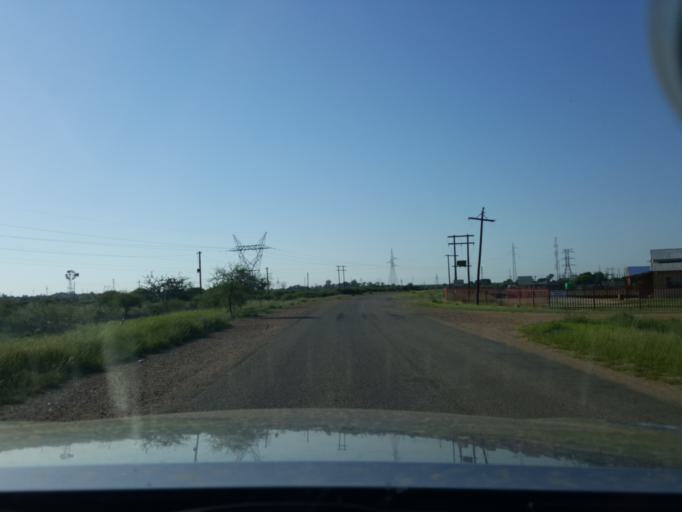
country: ZA
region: North-West
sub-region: Ngaka Modiri Molema District Municipality
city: Mahikeng
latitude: -25.8405
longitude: 25.6743
